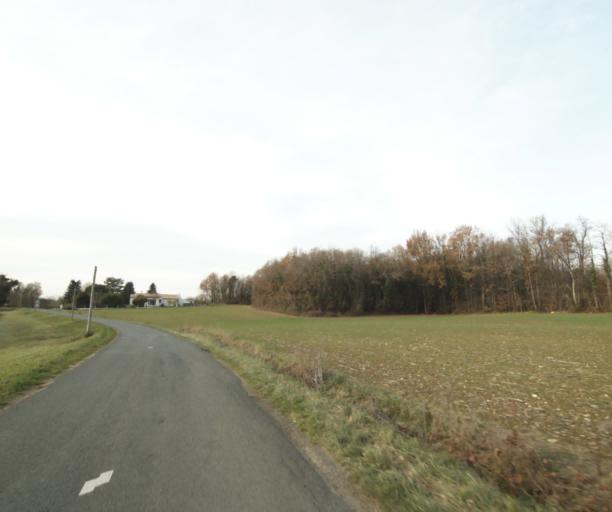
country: FR
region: Poitou-Charentes
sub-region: Departement de la Charente-Maritime
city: Saint-Hilaire-de-Villefranche
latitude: 45.8176
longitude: -0.5539
